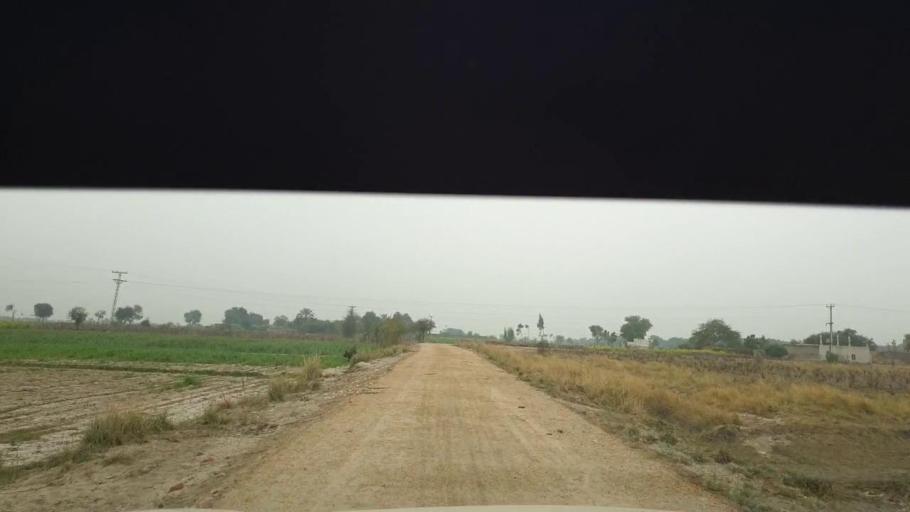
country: PK
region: Sindh
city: Berani
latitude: 25.7687
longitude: 68.7645
